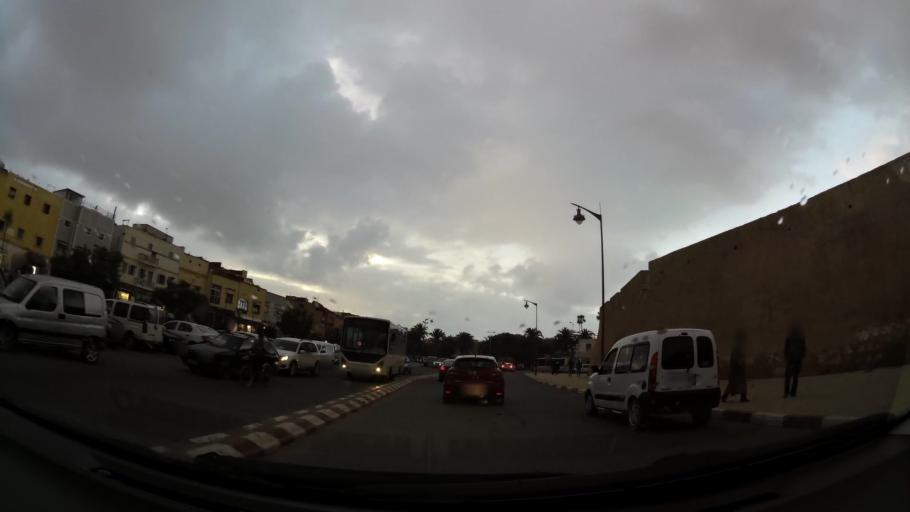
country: MA
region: Doukkala-Abda
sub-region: El-Jadida
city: El Jadida
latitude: 33.2567
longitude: -8.5043
